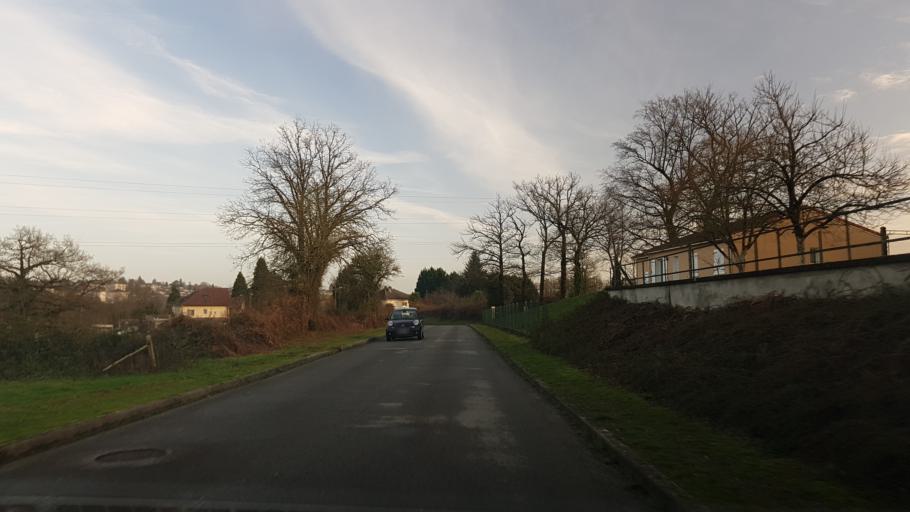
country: FR
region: Limousin
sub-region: Departement de la Haute-Vienne
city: Saint-Junien
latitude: 45.8930
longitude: 0.8787
